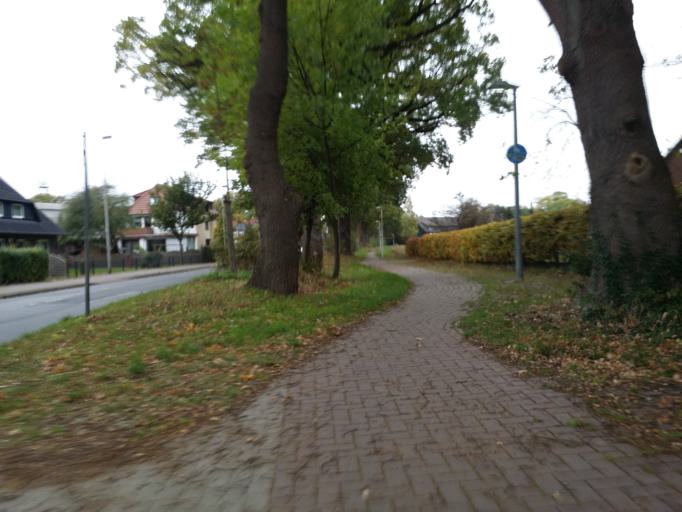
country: DE
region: Lower Saxony
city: Delmenhorst
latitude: 53.0542
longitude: 8.6789
